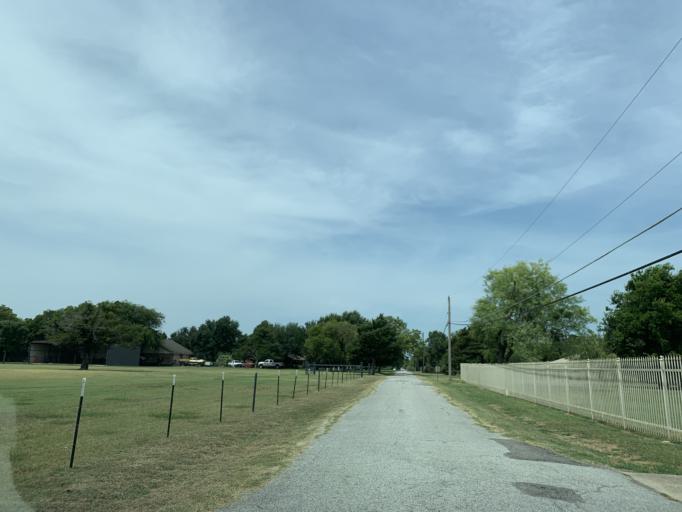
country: US
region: Texas
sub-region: Dallas County
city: Cedar Hill
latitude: 32.6543
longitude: -97.0009
